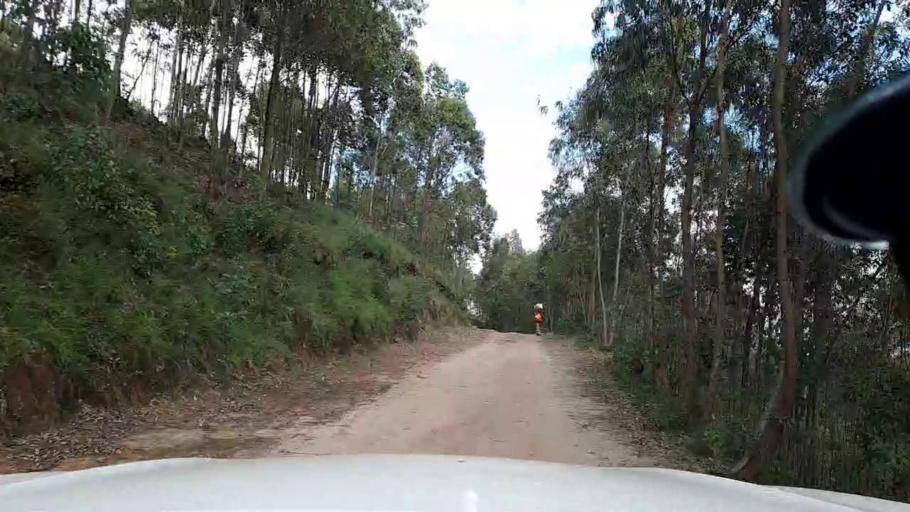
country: RW
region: Kigali
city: Kigali
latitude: -1.7829
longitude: 29.8341
